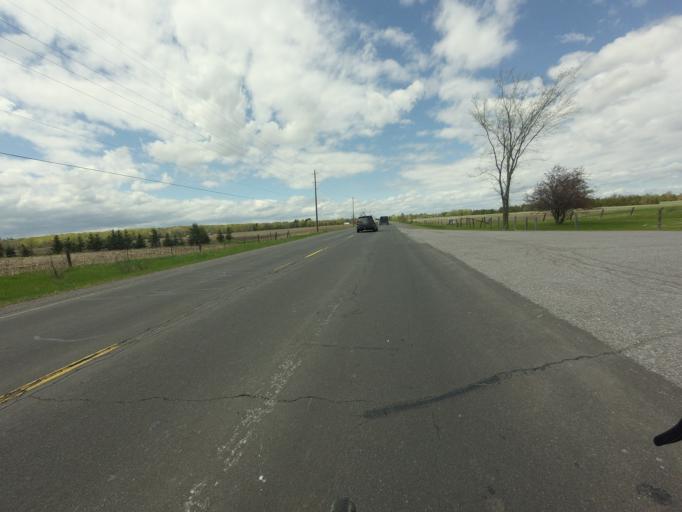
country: CA
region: Ontario
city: Carleton Place
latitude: 45.2488
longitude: -76.2413
